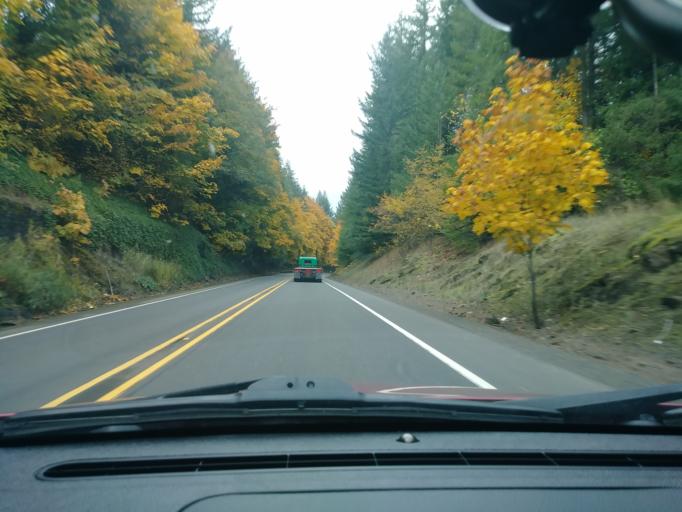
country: US
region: Oregon
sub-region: Washington County
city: Banks
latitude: 45.6411
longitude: -123.2674
